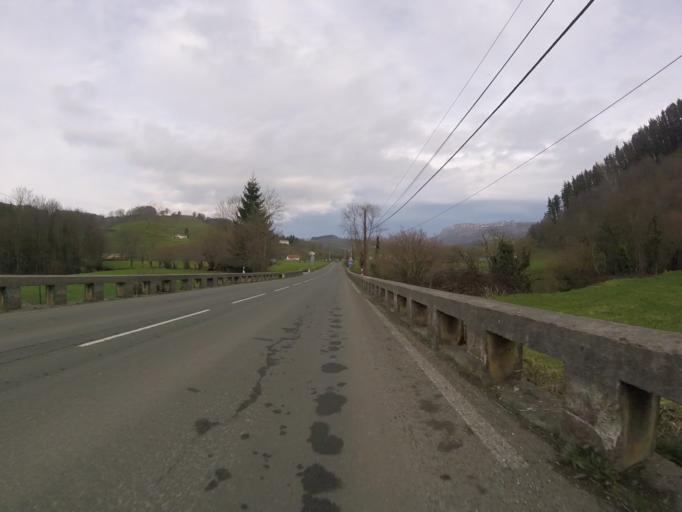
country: ES
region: Basque Country
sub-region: Provincia de Guipuzcoa
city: Albiztur
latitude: 43.1286
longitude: -2.1585
